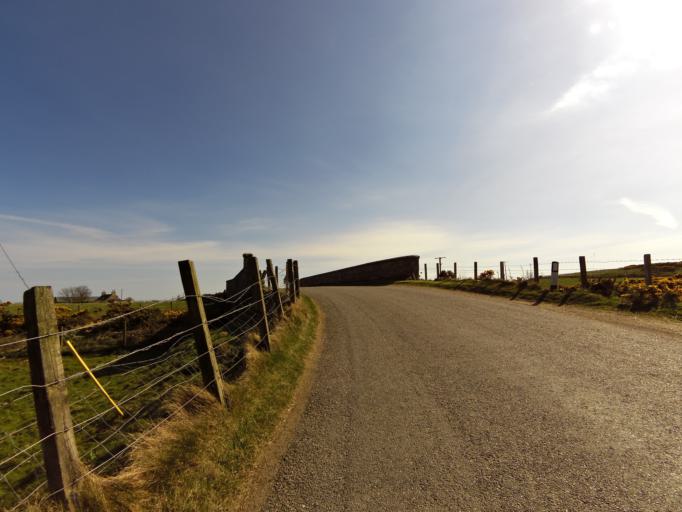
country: GB
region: Scotland
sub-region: Aberdeenshire
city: Portlethen
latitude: 57.0817
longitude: -2.1006
